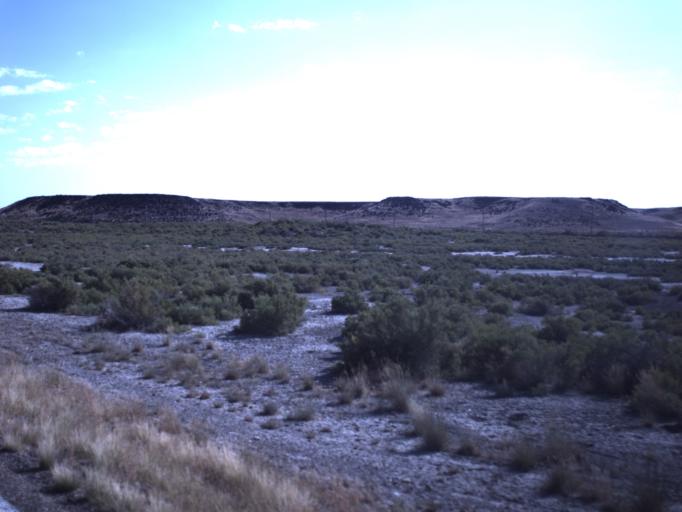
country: US
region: Utah
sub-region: Beaver County
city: Milford
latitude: 38.7229
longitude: -112.9680
